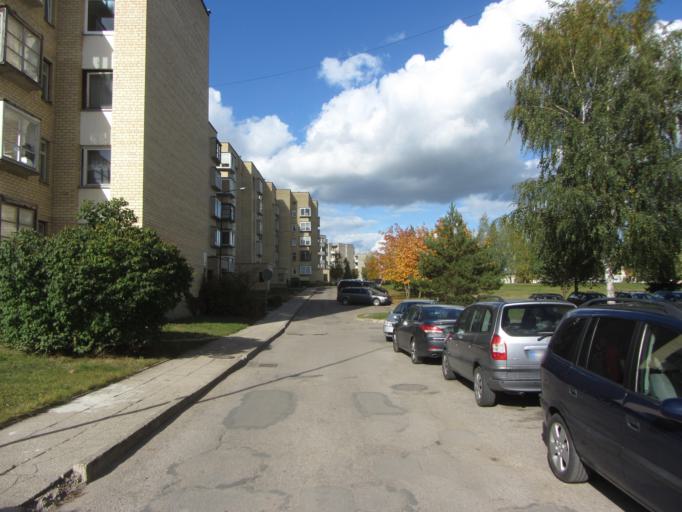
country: LT
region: Utenos apskritis
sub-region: Utena
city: Utena
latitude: 55.4943
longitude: 25.6157
